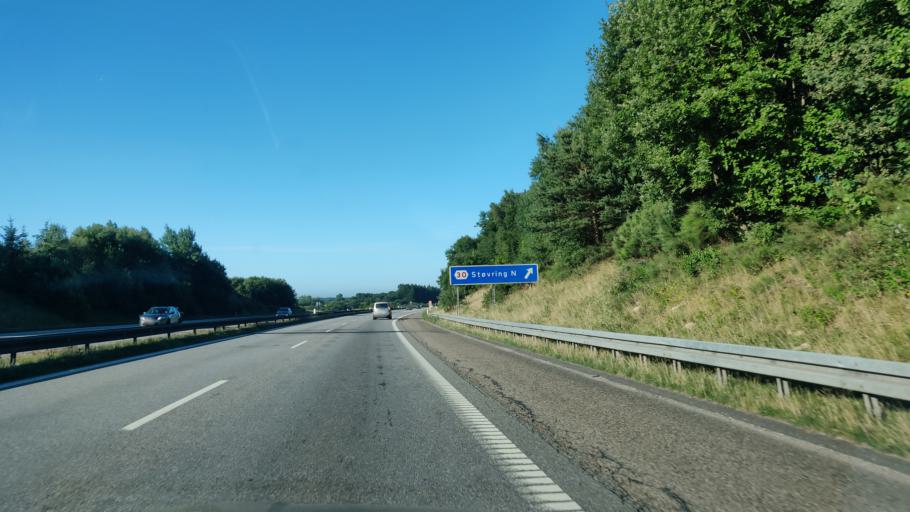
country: DK
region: North Denmark
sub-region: Rebild Kommune
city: Stovring
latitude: 56.9096
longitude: 9.8389
